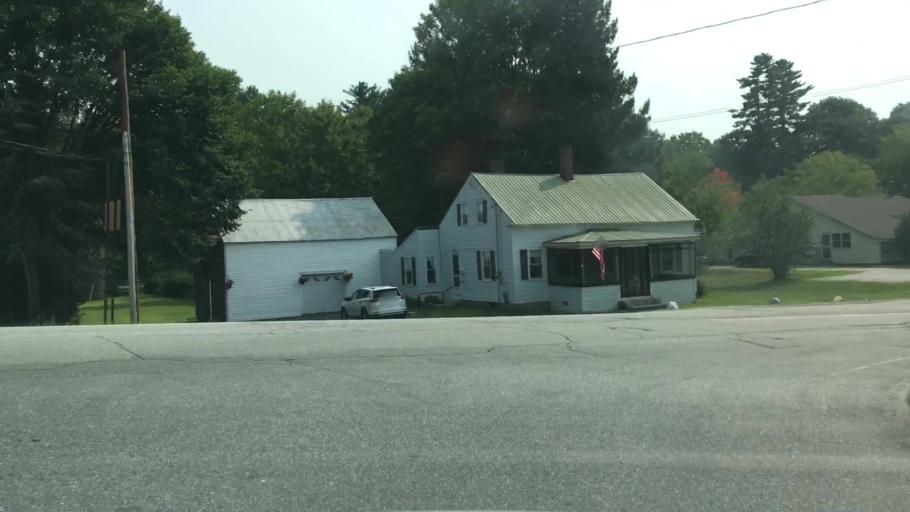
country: US
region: Maine
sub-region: Oxford County
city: South Paris
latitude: 44.2223
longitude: -70.5062
